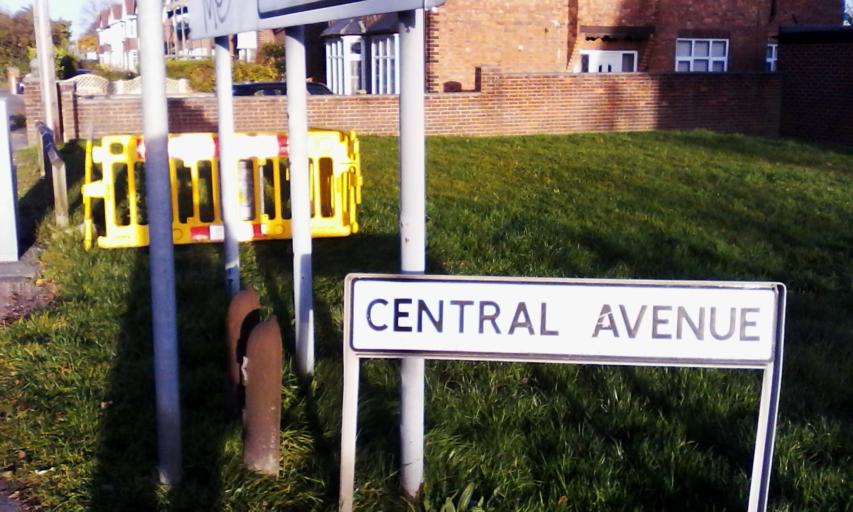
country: GB
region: England
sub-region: Nottinghamshire
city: Arnold
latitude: 52.9882
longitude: -1.1152
